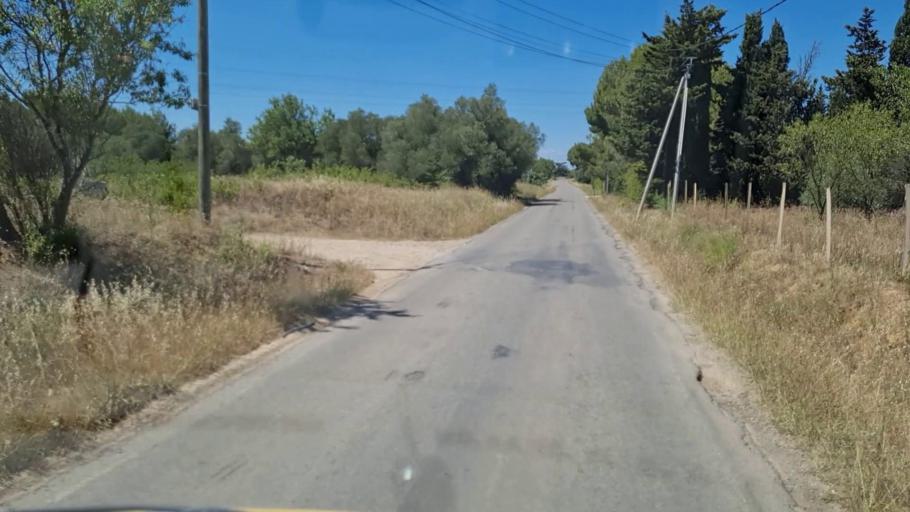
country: FR
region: Languedoc-Roussillon
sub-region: Departement du Gard
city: Codognan
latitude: 43.7217
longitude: 4.2250
